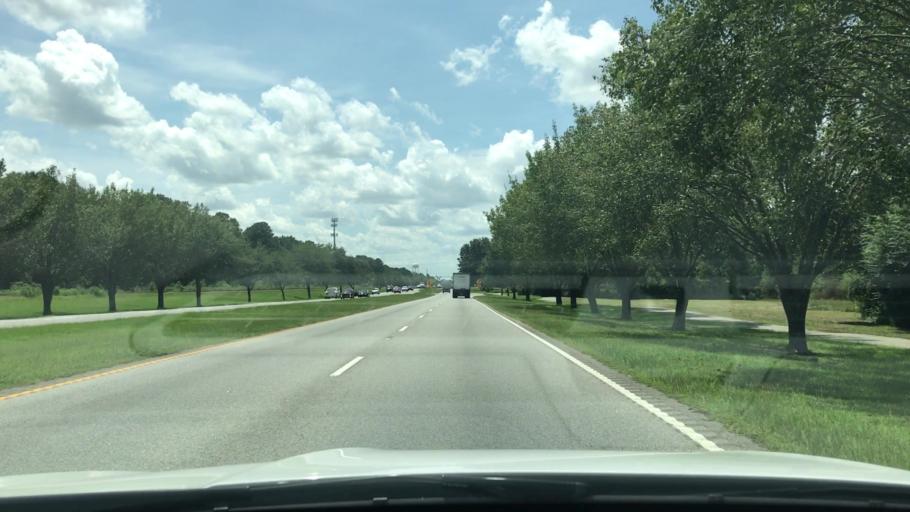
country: US
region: South Carolina
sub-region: Berkeley County
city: Goose Creek
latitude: 33.0228
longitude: -80.0357
